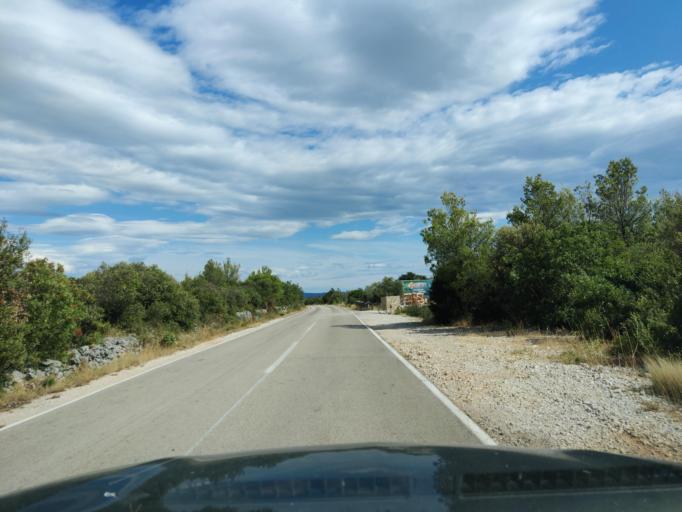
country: HR
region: Sibensko-Kniniska
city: Zaton
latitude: 43.7486
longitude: 15.8431
